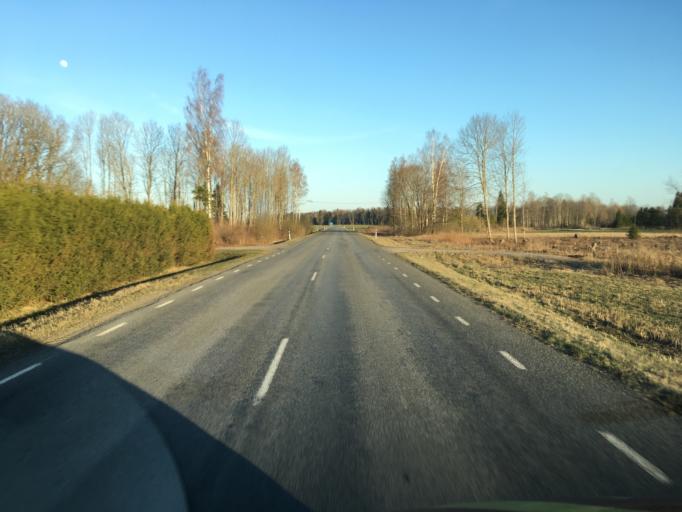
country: EE
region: Raplamaa
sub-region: Kehtna vald
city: Kehtna
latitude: 59.0601
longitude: 24.9386
